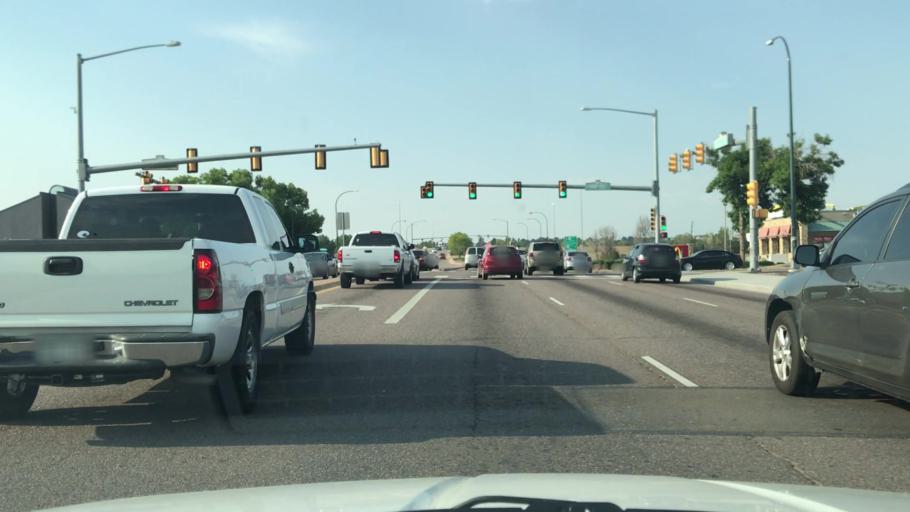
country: US
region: Colorado
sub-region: Adams County
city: Westminster
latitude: 39.8304
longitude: -105.0249
